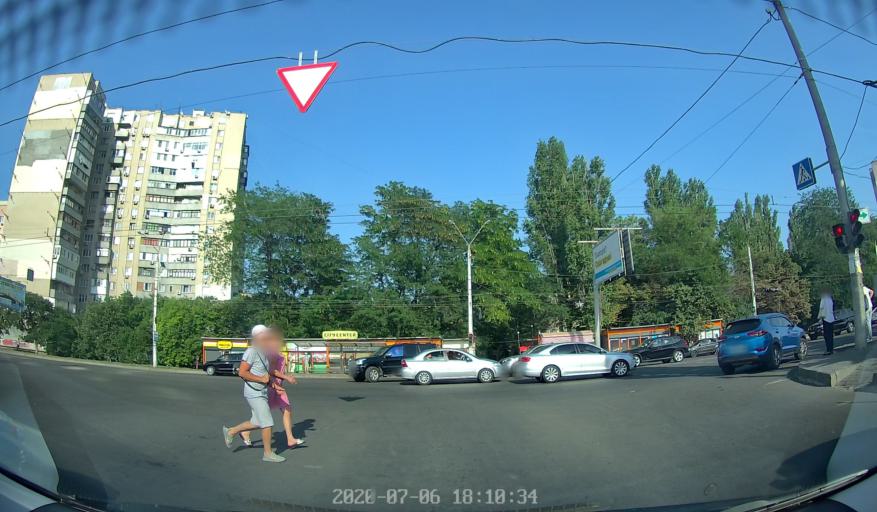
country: NG
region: Niger
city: Lemu
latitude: 9.2833
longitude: 6.1428
